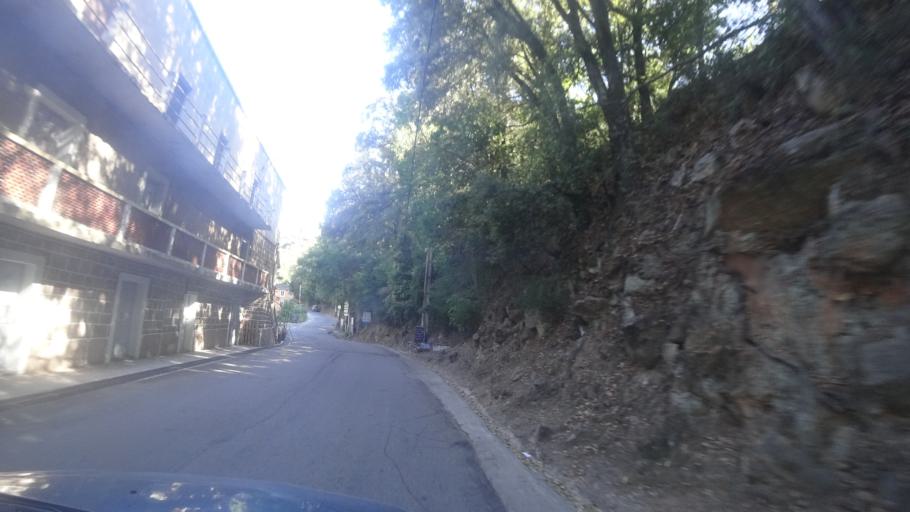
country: FR
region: Corsica
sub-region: Departement de la Corse-du-Sud
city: Cargese
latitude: 42.2620
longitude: 8.7089
